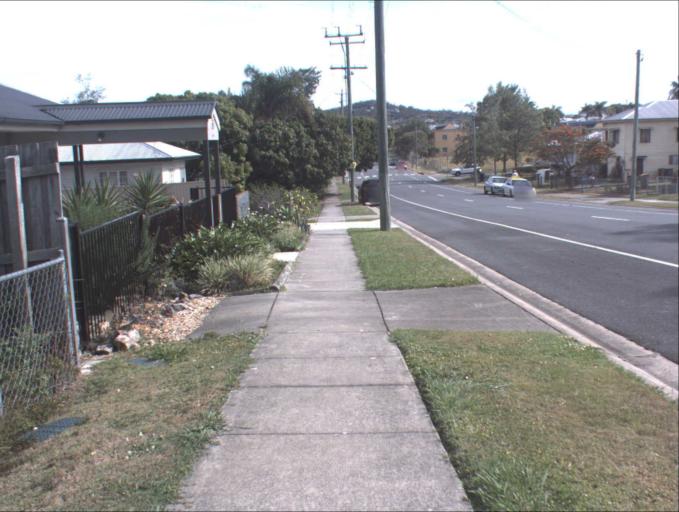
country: AU
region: Queensland
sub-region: Logan
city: Beenleigh
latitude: -27.7109
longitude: 153.2021
